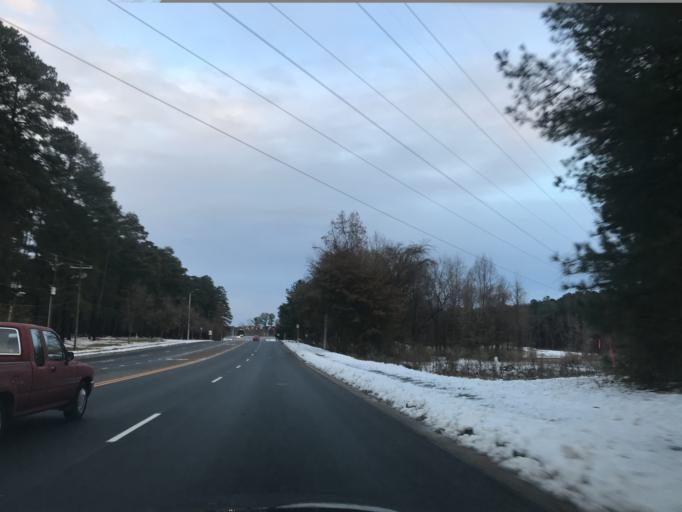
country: US
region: North Carolina
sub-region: Wake County
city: Wake Forest
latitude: 35.8949
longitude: -78.5639
